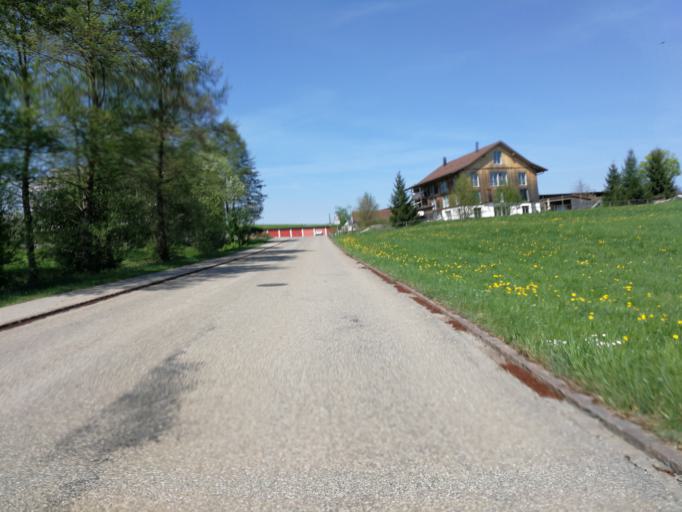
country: CH
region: Zurich
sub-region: Bezirk Hinwil
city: Bubikon
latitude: 47.2796
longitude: 8.8194
